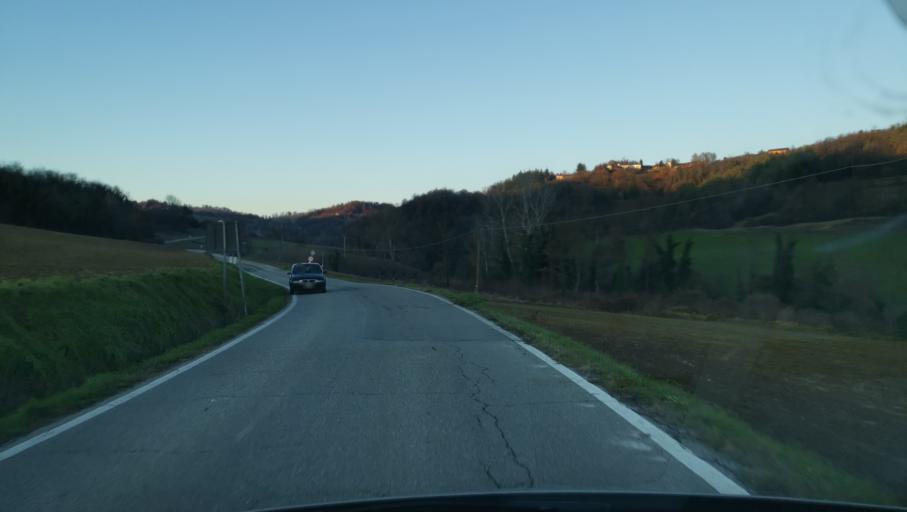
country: IT
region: Piedmont
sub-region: Provincia di Asti
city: Moncucco Torinese
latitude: 45.0706
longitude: 7.9417
